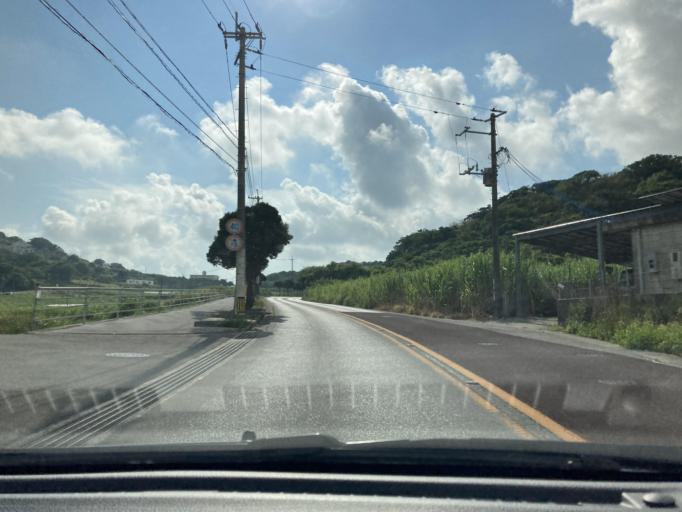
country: JP
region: Okinawa
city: Tomigusuku
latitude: 26.1497
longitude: 127.7536
